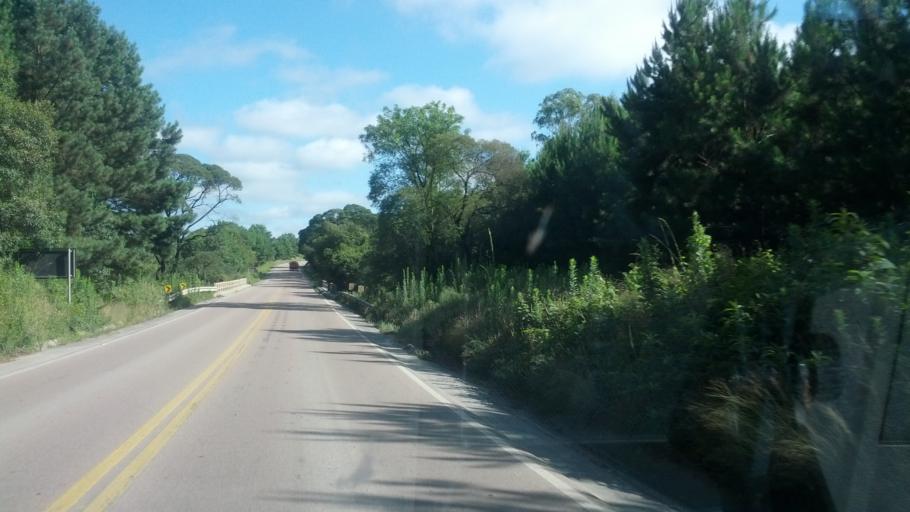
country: BR
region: Santa Catarina
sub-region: Otacilio Costa
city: Otacilio Costa
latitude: -27.4646
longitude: -50.1226
